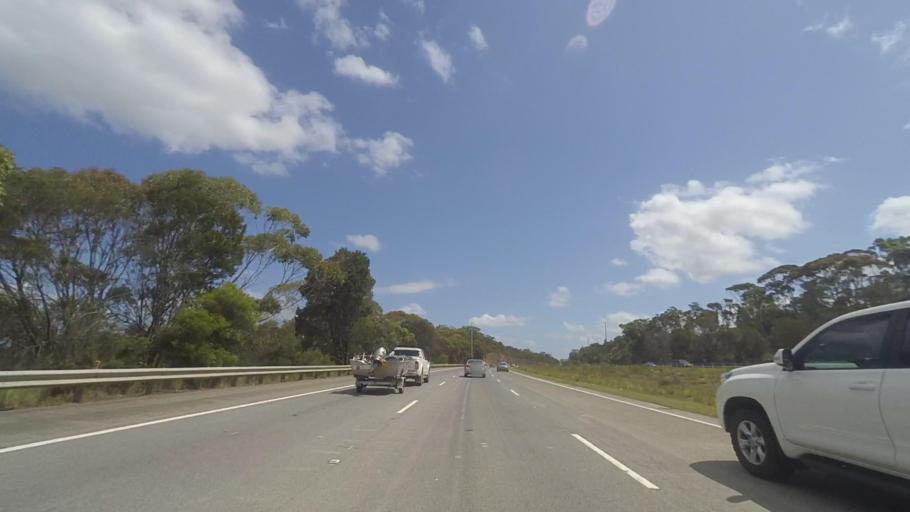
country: AU
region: New South Wales
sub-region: Hornsby Shire
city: Berowra
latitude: -33.6164
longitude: 151.1606
